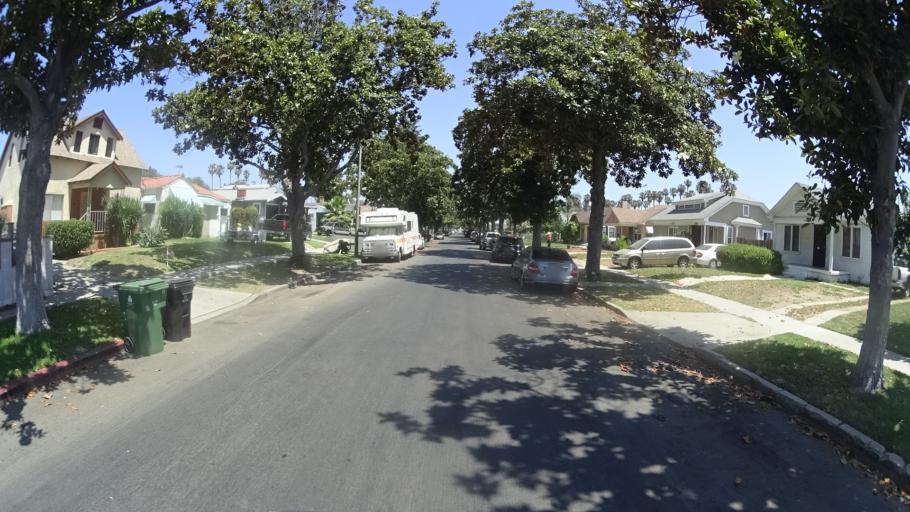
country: US
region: California
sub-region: Los Angeles County
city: View Park-Windsor Hills
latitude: 33.9951
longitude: -118.3247
